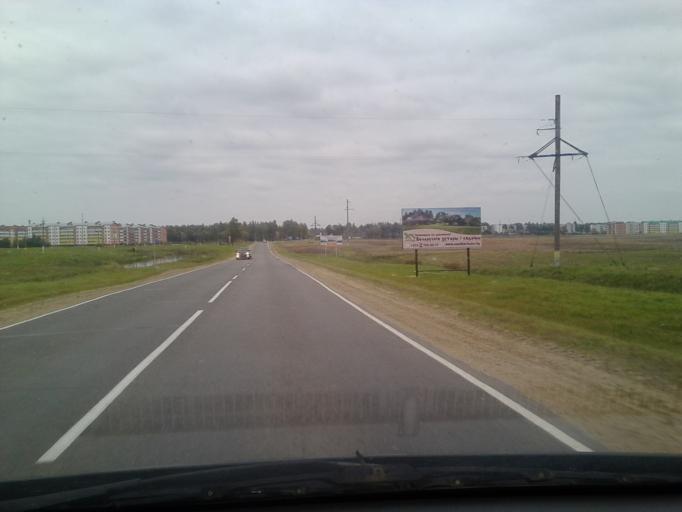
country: BY
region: Vitebsk
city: Pastavy
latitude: 55.1039
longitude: 26.8747
